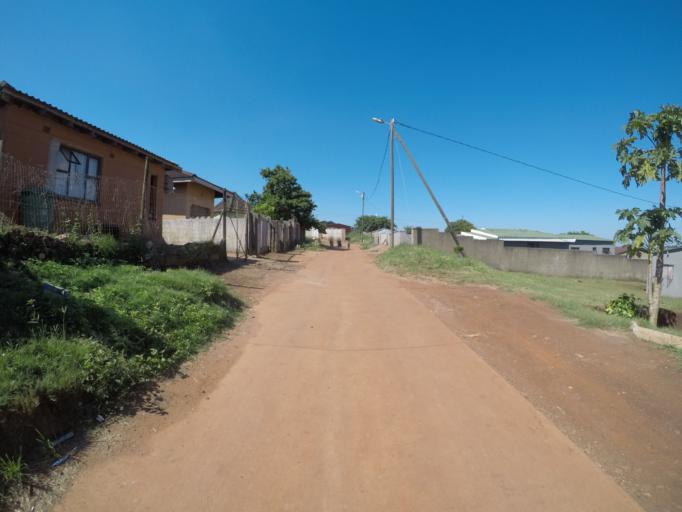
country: ZA
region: KwaZulu-Natal
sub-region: uThungulu District Municipality
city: Empangeni
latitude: -28.7756
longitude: 31.8784
